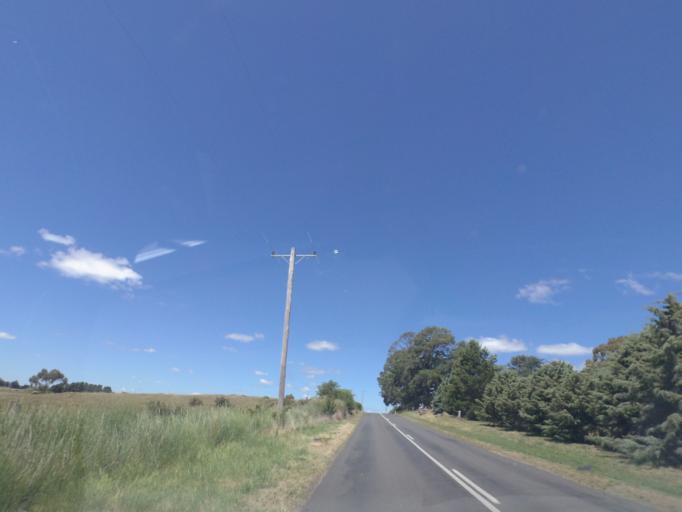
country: AU
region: Victoria
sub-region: Mount Alexander
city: Castlemaine
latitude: -37.2361
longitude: 144.3999
